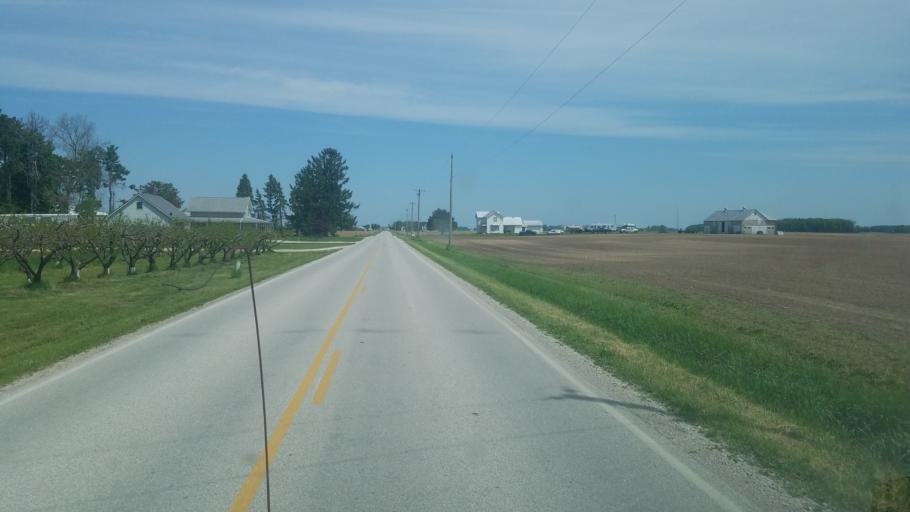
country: US
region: Ohio
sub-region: Sandusky County
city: Green Springs
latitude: 41.2475
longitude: -83.1313
